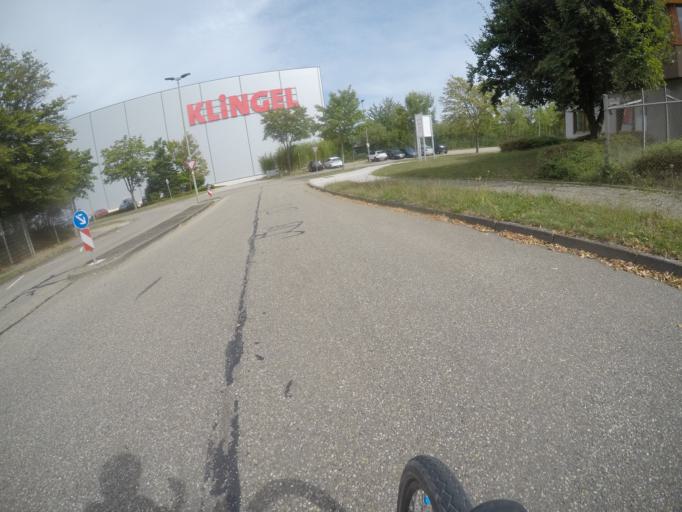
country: DE
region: Baden-Wuerttemberg
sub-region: Karlsruhe Region
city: Eutingen
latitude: 48.8874
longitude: 8.7541
